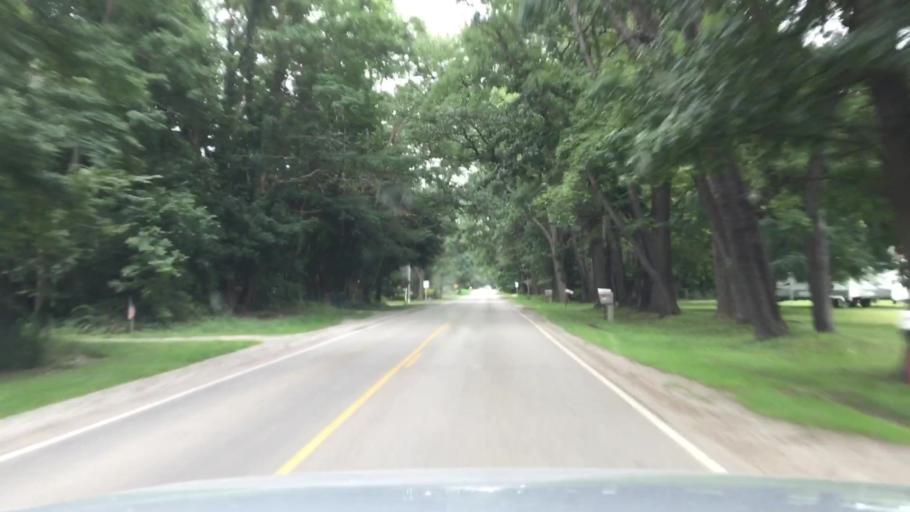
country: US
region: Michigan
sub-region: Genesee County
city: Argentine
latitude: 42.8107
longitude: -83.8910
